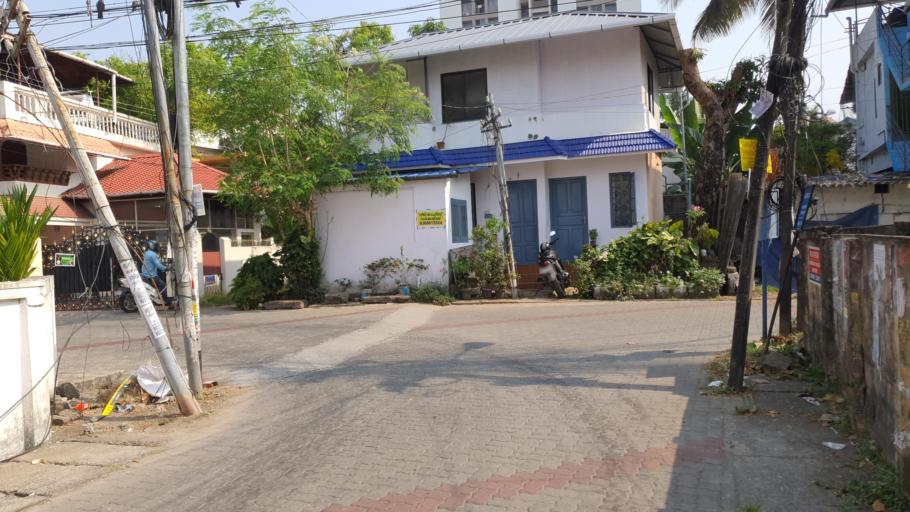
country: IN
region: Kerala
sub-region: Ernakulam
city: Cochin
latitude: 9.9587
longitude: 76.3008
